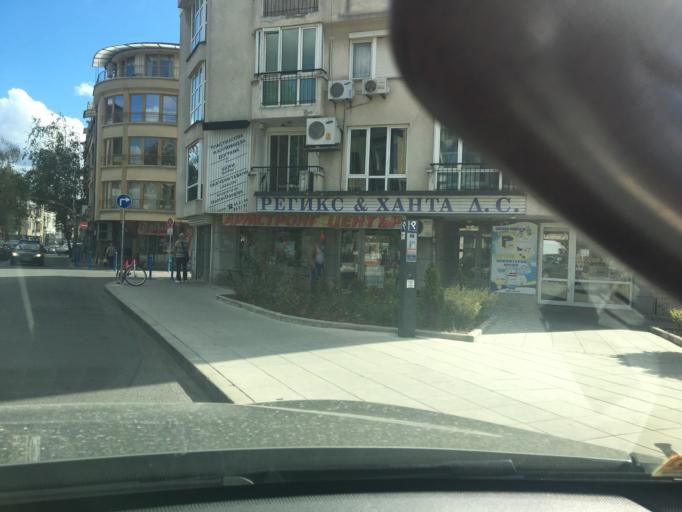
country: BG
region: Burgas
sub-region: Obshtina Burgas
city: Burgas
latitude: 42.4962
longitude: 27.4746
